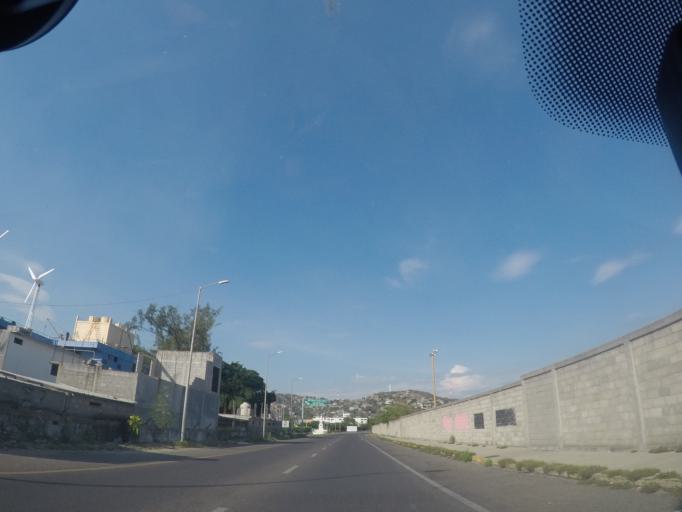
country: MX
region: Oaxaca
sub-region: Salina Cruz
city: Salina Cruz
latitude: 16.1740
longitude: -95.1965
